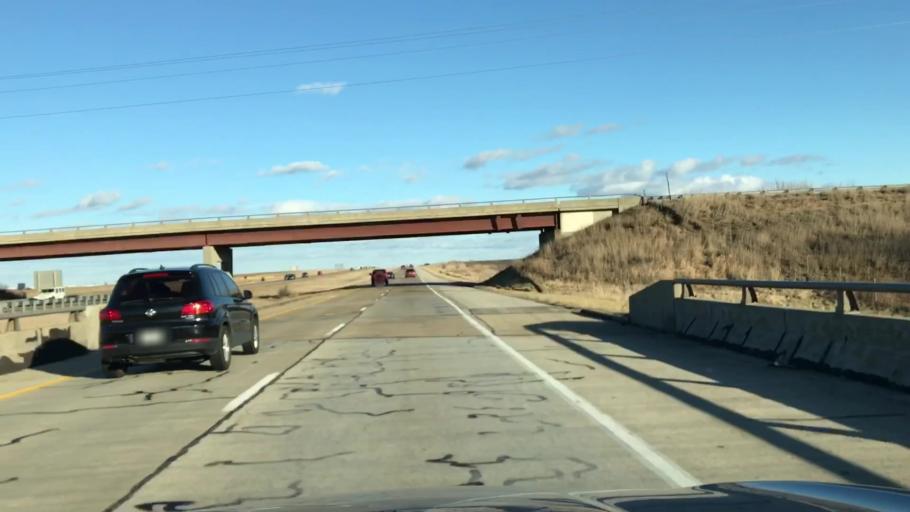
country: US
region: Illinois
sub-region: McLean County
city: Lexington
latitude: 40.6572
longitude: -88.7941
